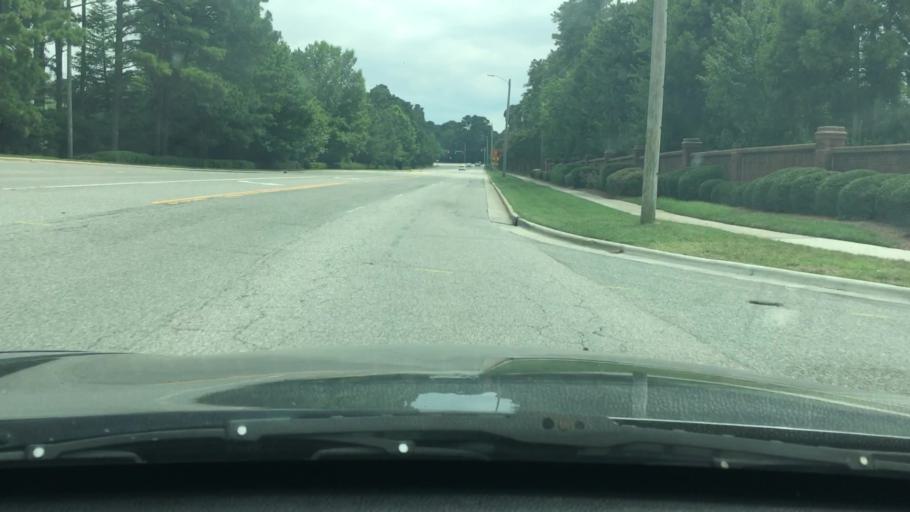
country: US
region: North Carolina
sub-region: Wake County
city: West Raleigh
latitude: 35.8307
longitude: -78.7105
